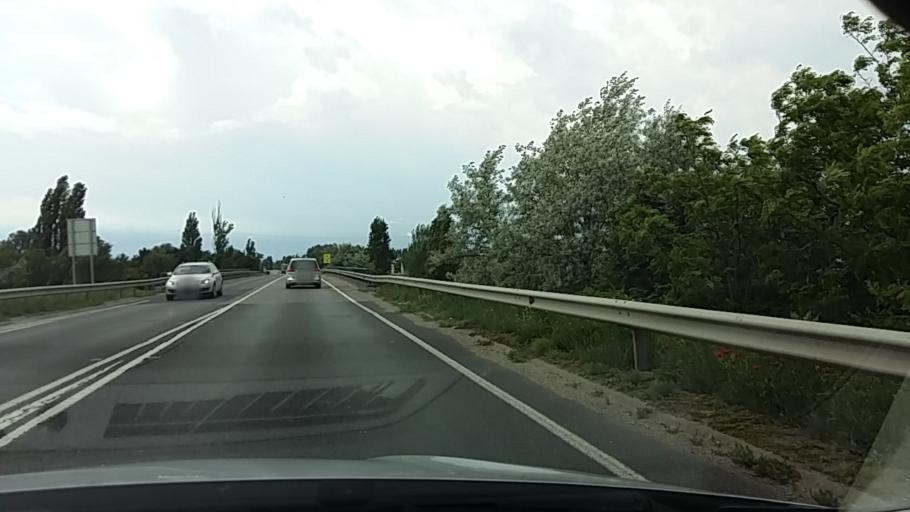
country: HU
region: Fejer
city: Pakozd
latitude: 47.1776
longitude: 18.4812
